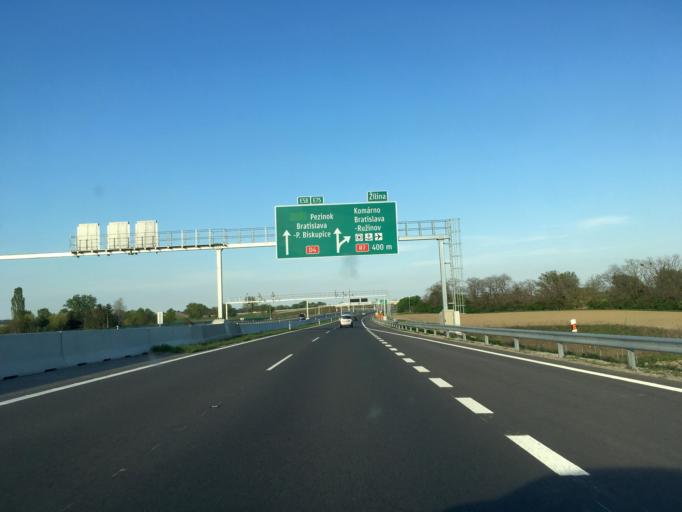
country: SK
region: Bratislavsky
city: Bratislava
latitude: 48.0885
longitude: 17.1718
